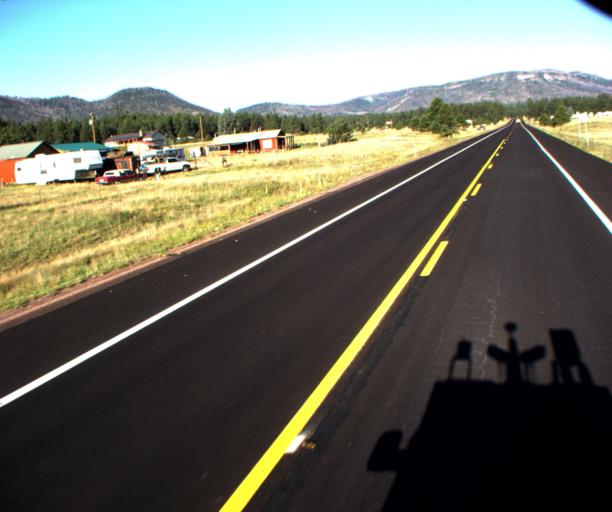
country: US
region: Arizona
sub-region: Apache County
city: Eagar
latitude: 33.8275
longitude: -109.1009
